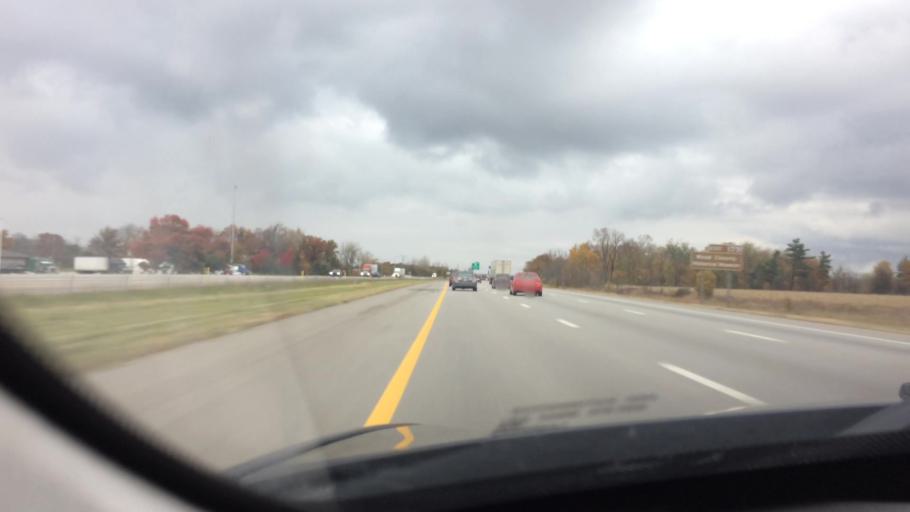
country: US
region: Ohio
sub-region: Wood County
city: Bowling Green
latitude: 41.3334
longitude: -83.6258
